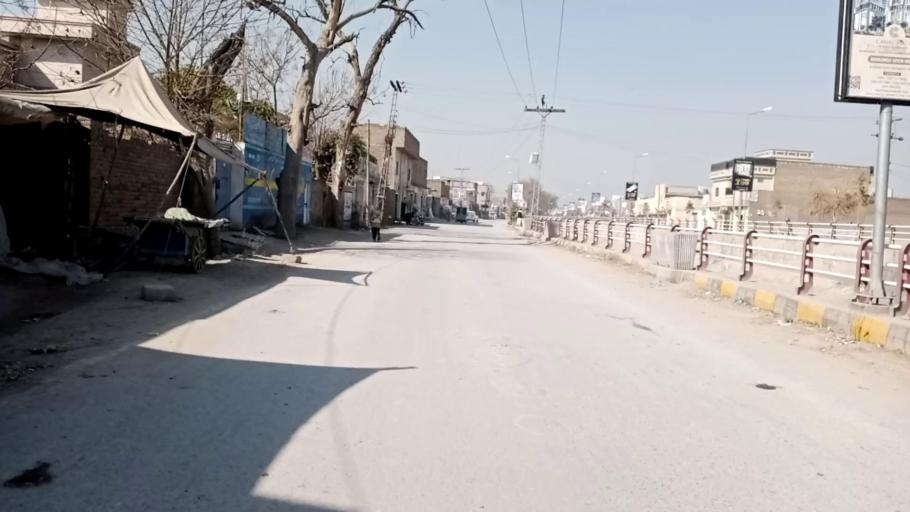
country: PK
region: Khyber Pakhtunkhwa
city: Peshawar
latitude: 33.9788
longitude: 71.5068
